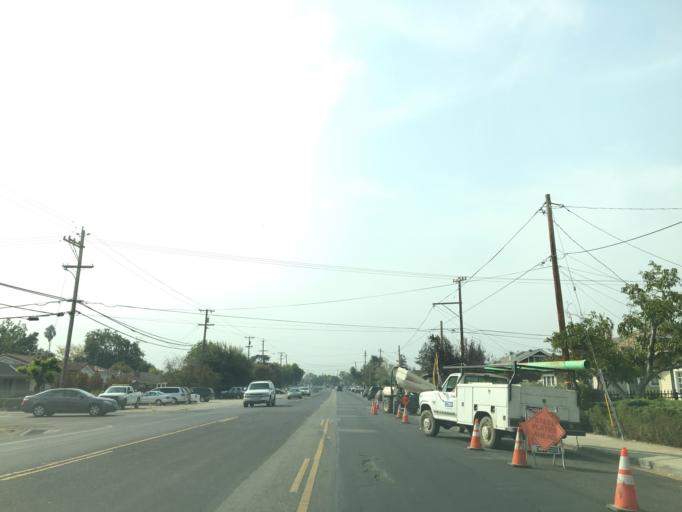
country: US
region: California
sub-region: Santa Clara County
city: Alum Rock
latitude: 37.3698
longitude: -121.8251
